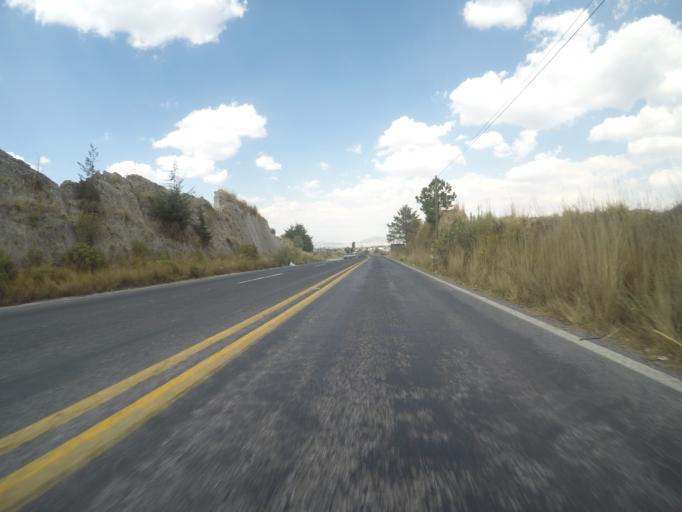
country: MX
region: Mexico
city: San Juan de las Huertas
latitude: 19.2261
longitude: -99.7868
